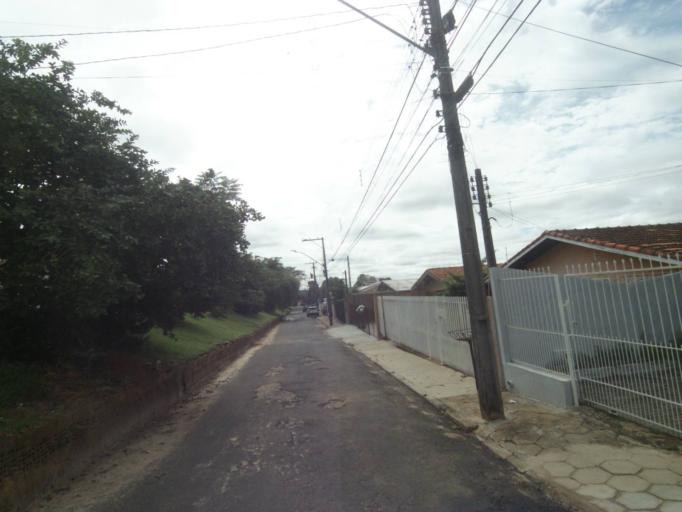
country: BR
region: Parana
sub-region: Telemaco Borba
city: Telemaco Borba
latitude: -24.3338
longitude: -50.6241
